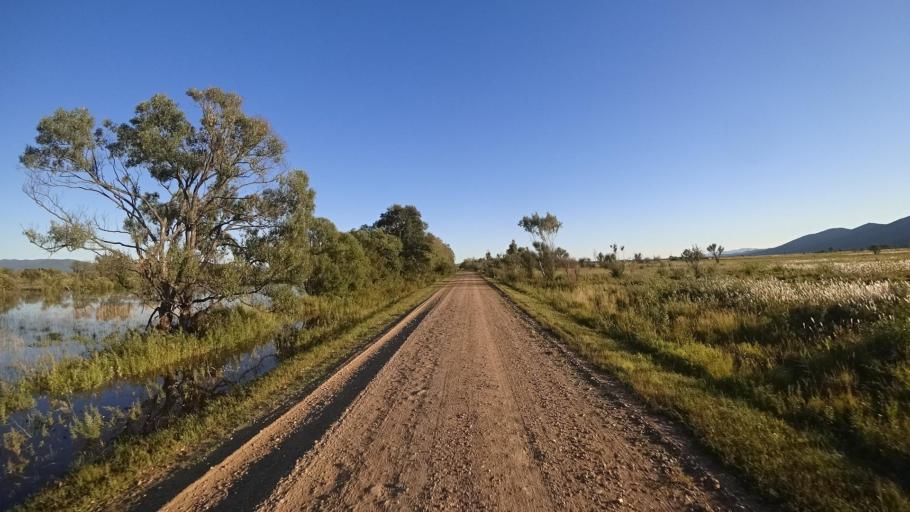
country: RU
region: Primorskiy
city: Kirovskiy
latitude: 44.8112
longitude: 133.6163
